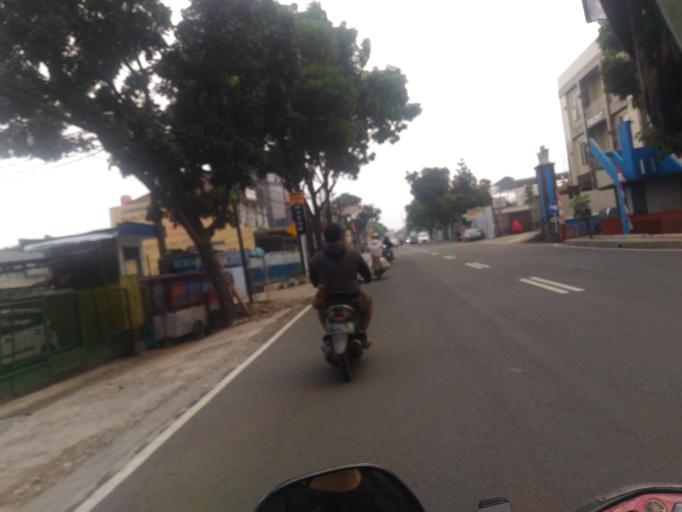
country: ID
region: West Java
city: Bogor
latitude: -6.6298
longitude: 106.8242
